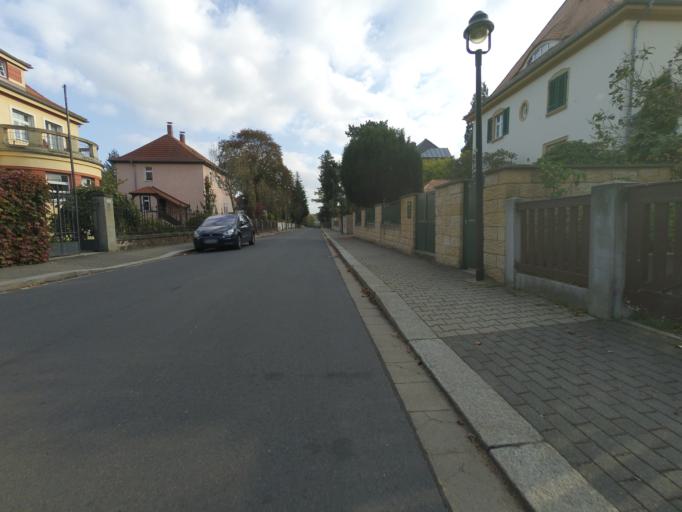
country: DE
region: Saxony
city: Albertstadt
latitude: 51.0643
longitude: 13.8441
